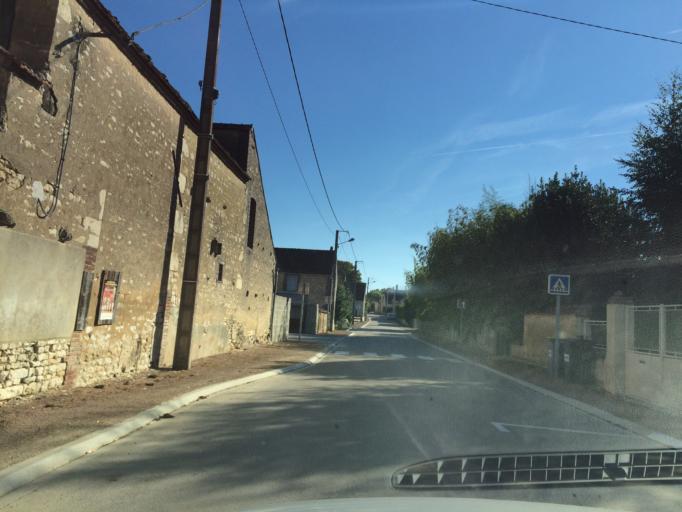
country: FR
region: Bourgogne
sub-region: Departement de l'Yonne
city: Fleury-la-Vallee
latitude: 47.8981
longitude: 3.4443
